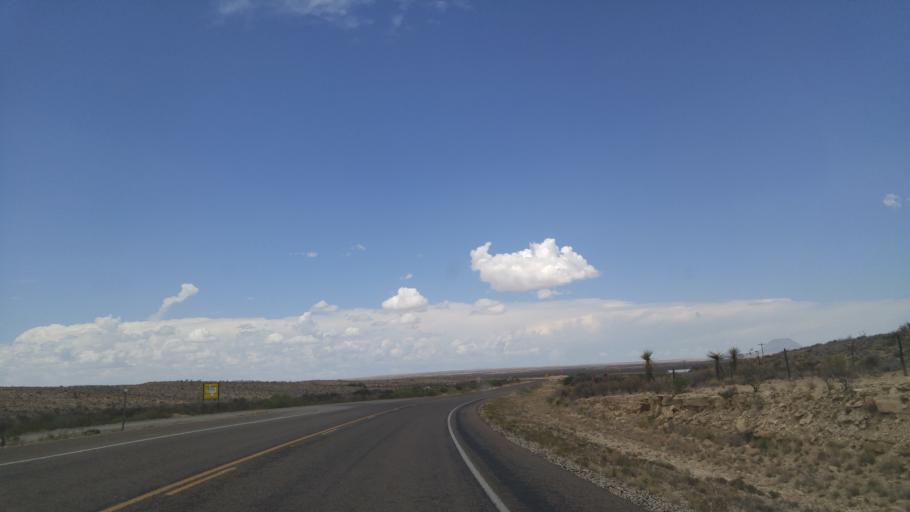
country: US
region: Texas
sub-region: Brewster County
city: Alpine
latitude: 29.5920
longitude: -103.5609
